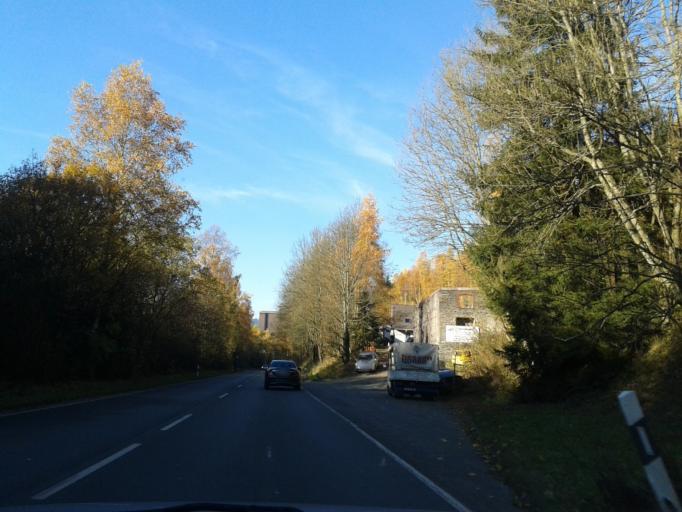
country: DE
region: North Rhine-Westphalia
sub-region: Regierungsbezirk Arnsberg
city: Bad Berleburg
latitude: 51.0215
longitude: 8.3720
